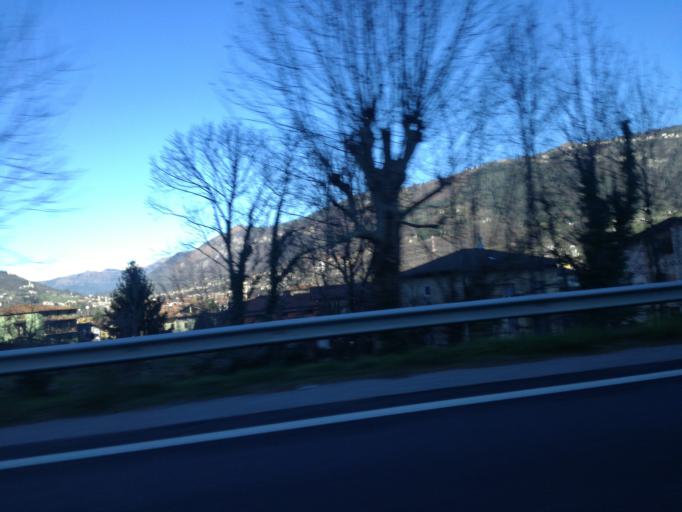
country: IT
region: Lombardy
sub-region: Provincia di Bergamo
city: Sovere
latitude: 45.8078
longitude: 10.0303
